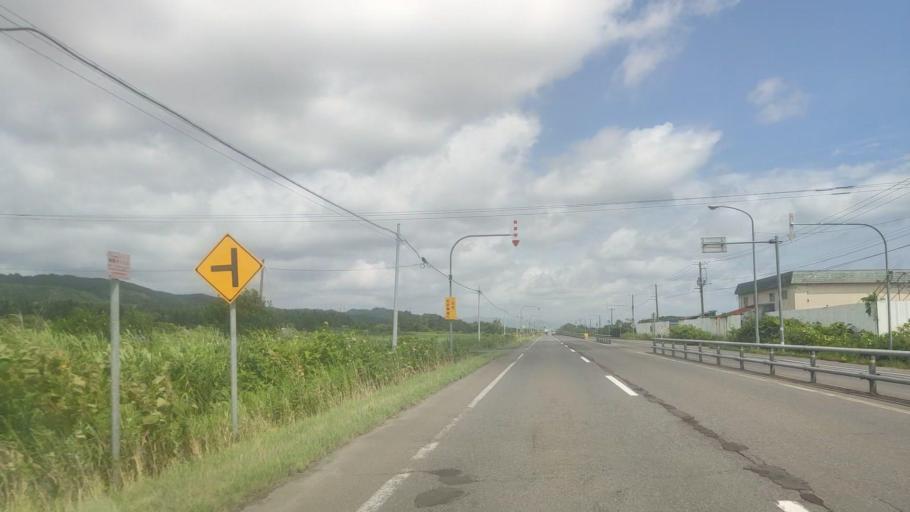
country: JP
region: Hokkaido
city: Niseko Town
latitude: 42.4135
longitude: 140.3085
